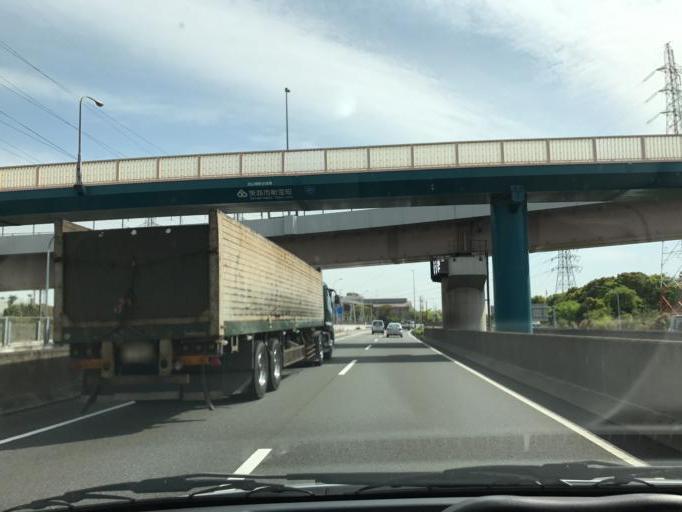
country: JP
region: Aichi
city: Obu
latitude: 35.0513
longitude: 136.9007
